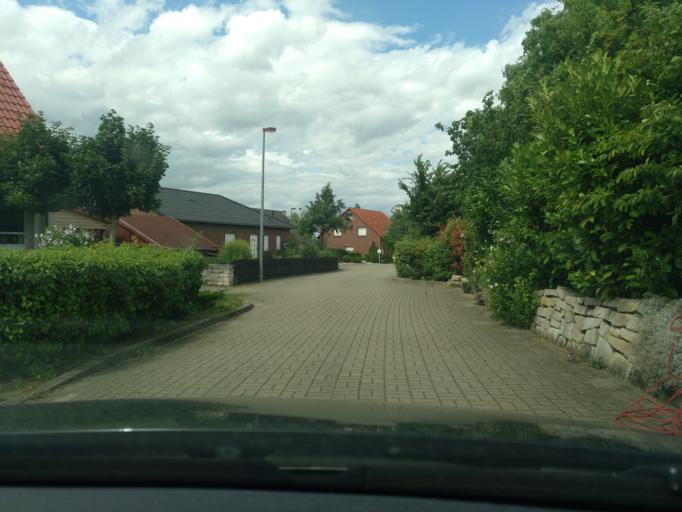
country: DE
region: Lower Saxony
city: Sickte
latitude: 52.1941
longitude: 10.6230
